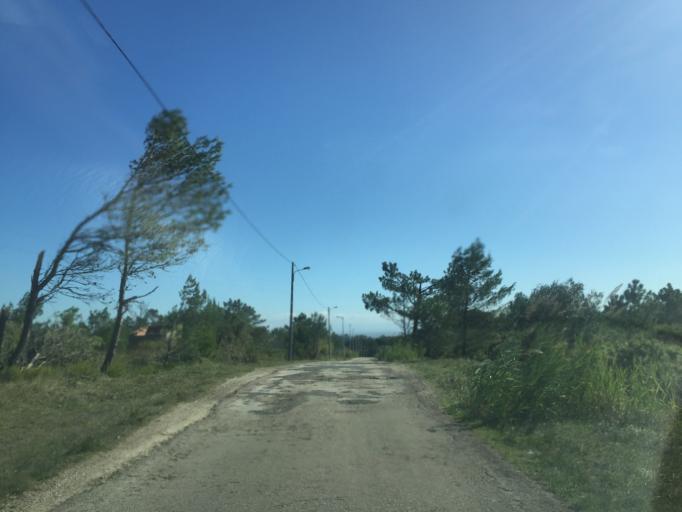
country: PT
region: Coimbra
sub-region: Figueira da Foz
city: Tavarede
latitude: 40.1906
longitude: -8.8350
